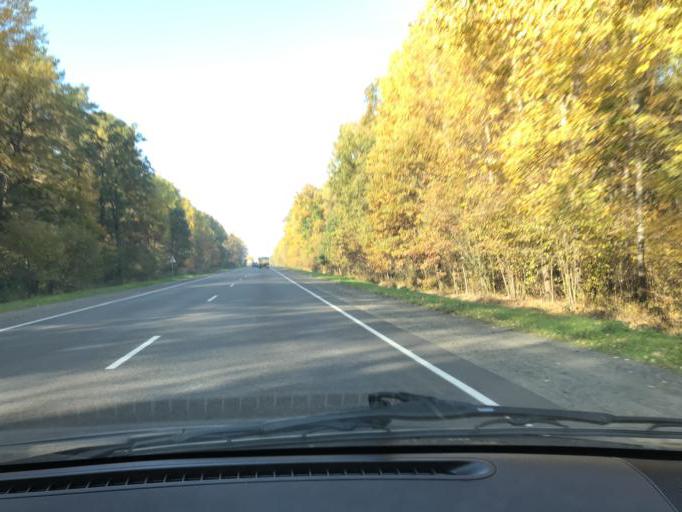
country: BY
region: Brest
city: Horad Luninyets
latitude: 52.3081
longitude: 26.6829
